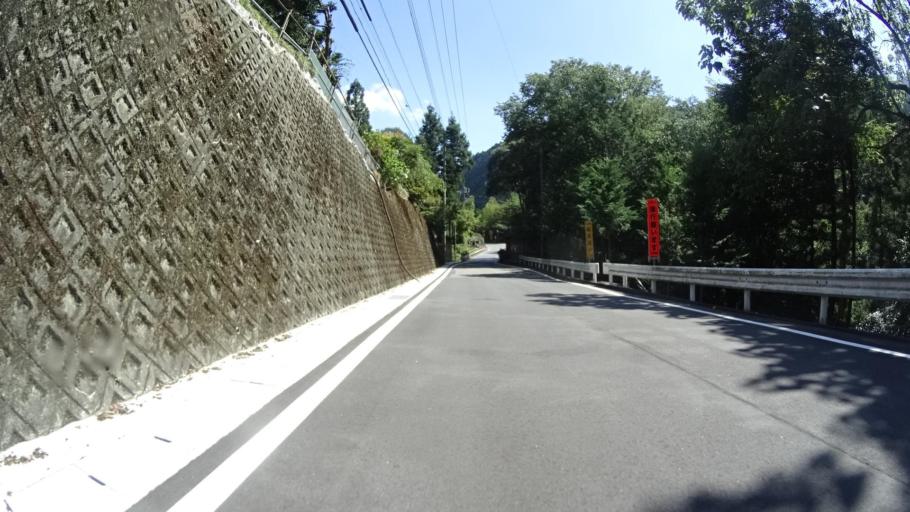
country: JP
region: Yamanashi
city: Uenohara
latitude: 35.6836
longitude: 139.0607
